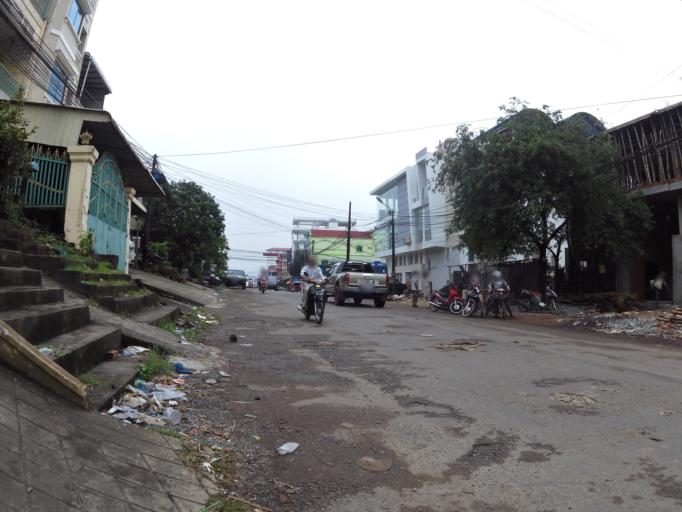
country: KH
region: Preah Sihanouk
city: Sihanoukville
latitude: 10.6256
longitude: 103.5259
